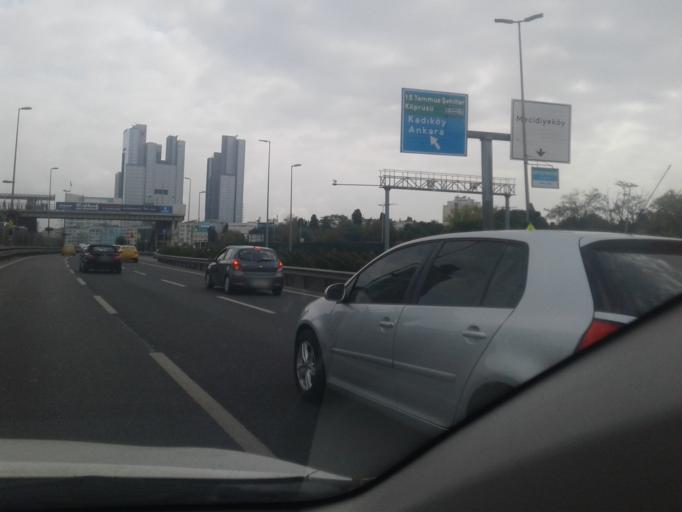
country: TR
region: Istanbul
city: Sisli
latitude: 41.0670
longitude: 28.9892
